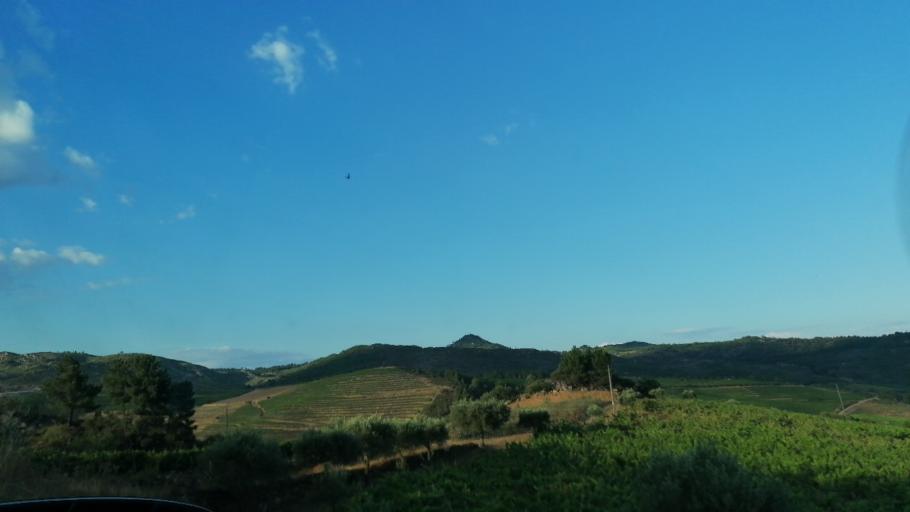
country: PT
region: Vila Real
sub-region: Sabrosa
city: Sabrosa
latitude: 41.2684
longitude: -7.4556
